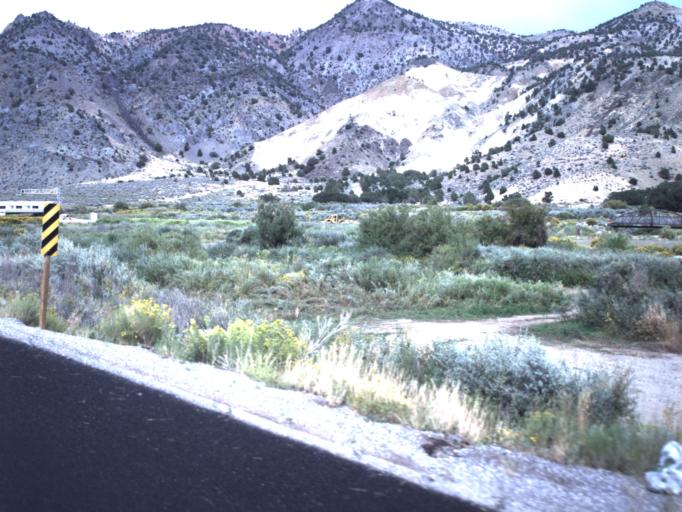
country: US
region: Utah
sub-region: Sevier County
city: Monroe
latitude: 38.5181
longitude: -112.2665
